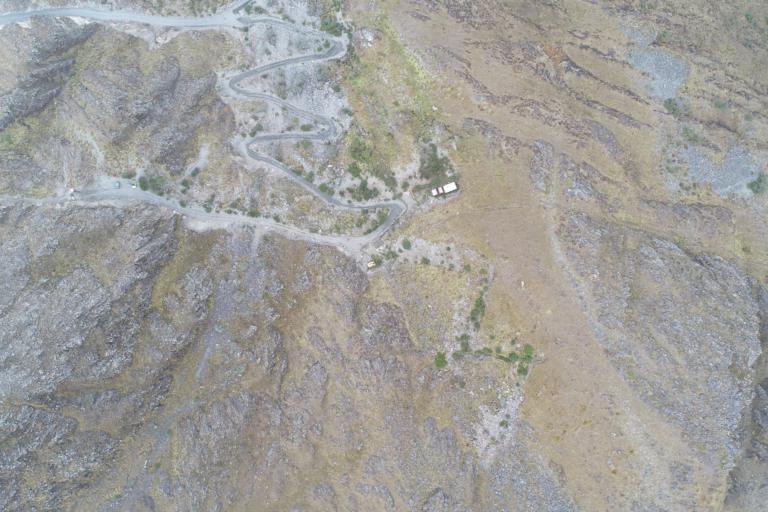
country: BO
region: La Paz
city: Sorata
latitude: -15.6568
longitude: -68.5344
